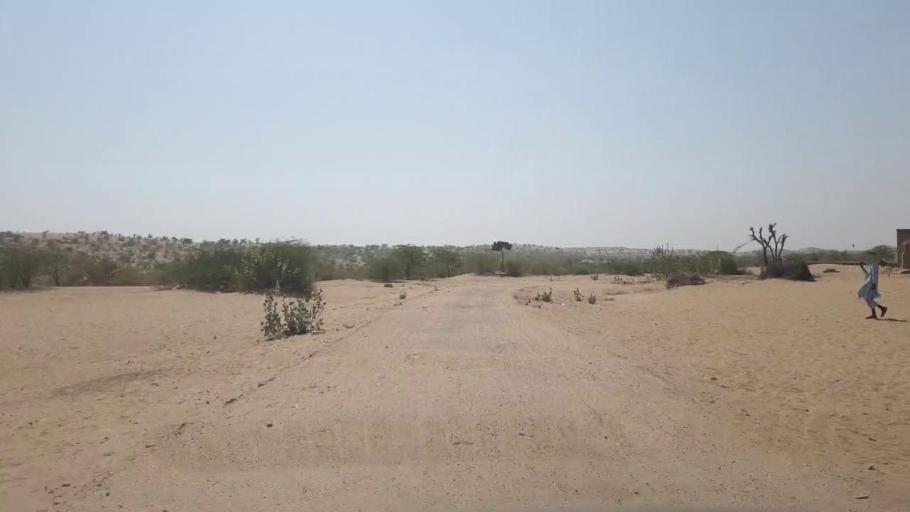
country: PK
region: Sindh
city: Chor
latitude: 25.5625
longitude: 70.1787
